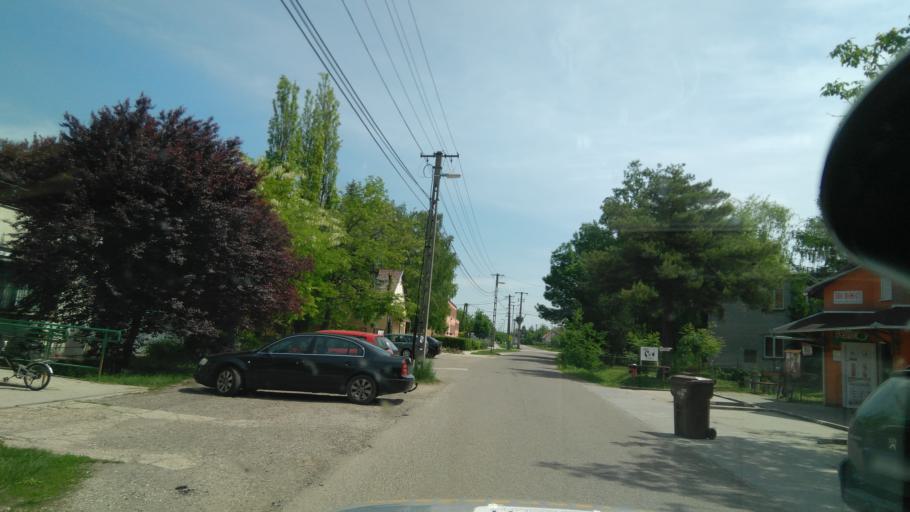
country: HU
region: Csongrad
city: Szekkutas
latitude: 46.5839
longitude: 20.4818
